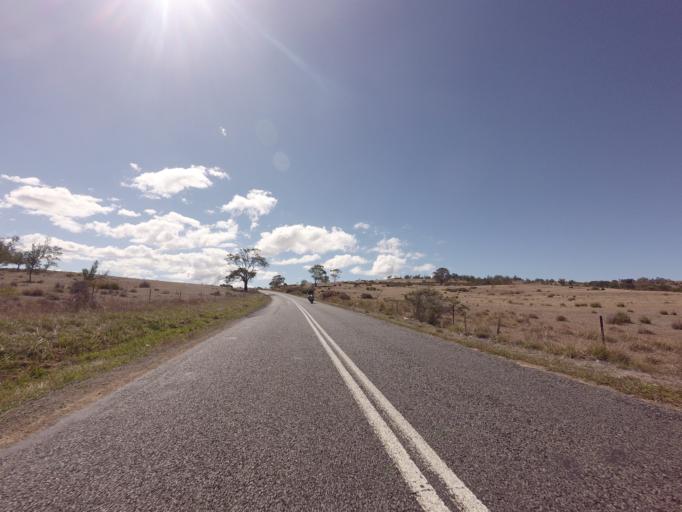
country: AU
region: Tasmania
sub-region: Break O'Day
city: St Helens
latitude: -41.9973
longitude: 148.0916
